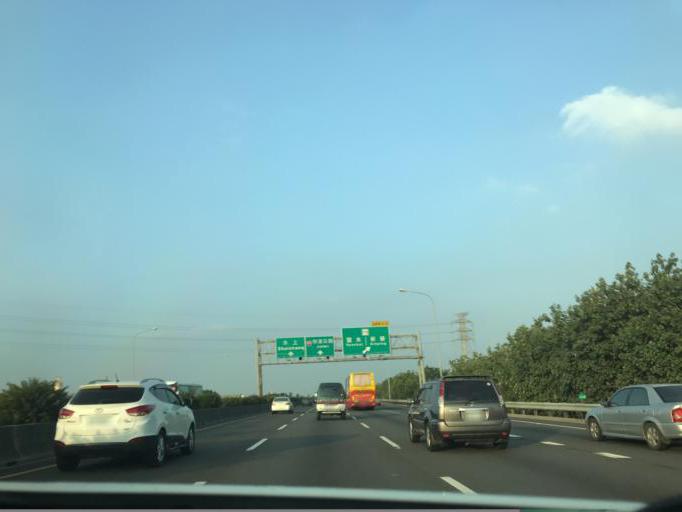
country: TW
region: Taiwan
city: Xinying
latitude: 23.2992
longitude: 120.2850
